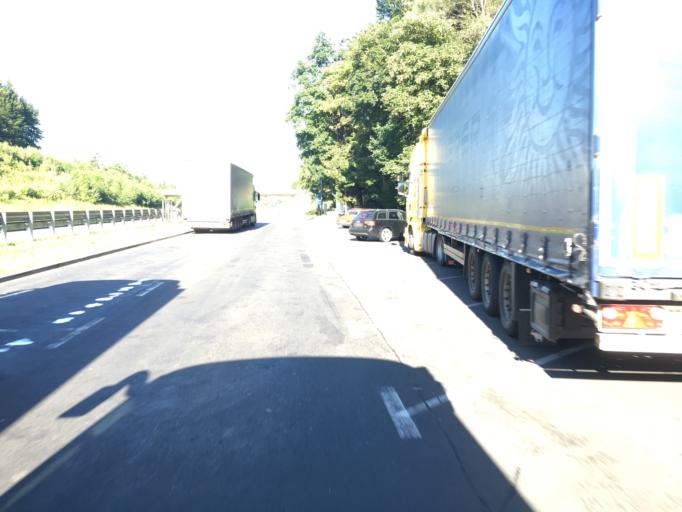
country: SI
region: Celje
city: Ljubecna
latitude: 46.2582
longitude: 15.3674
